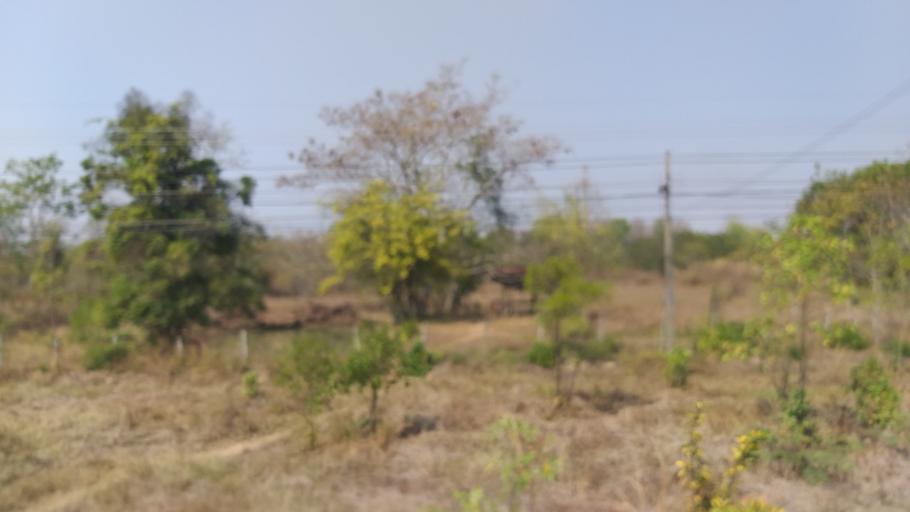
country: TH
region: Changwat Udon Thani
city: Ban Na Muang
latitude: 17.3539
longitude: 102.9329
